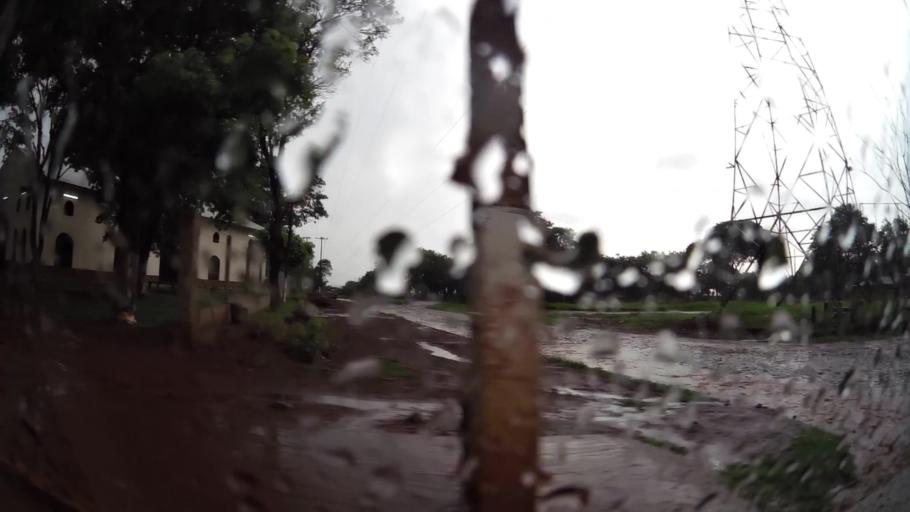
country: PY
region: Alto Parana
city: Presidente Franco
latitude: -25.5495
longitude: -54.6715
